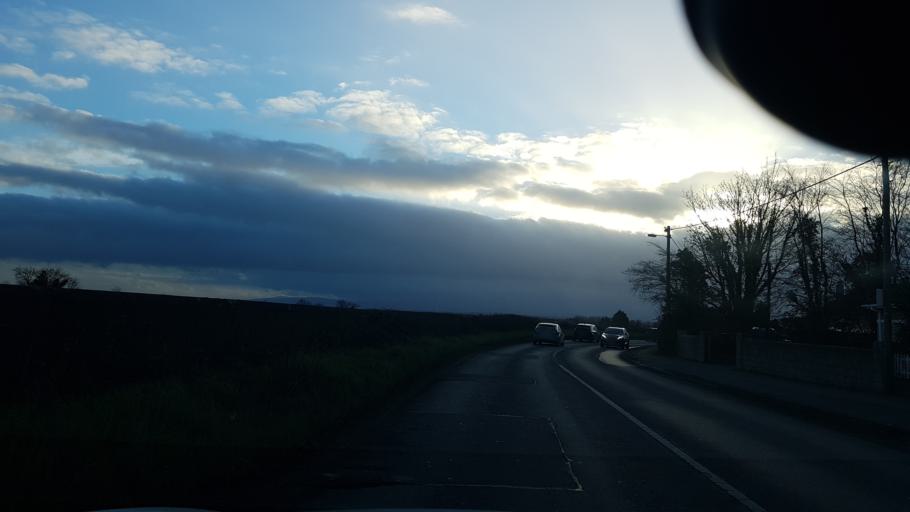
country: IE
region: Leinster
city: Lusk
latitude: 53.5113
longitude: -6.1778
